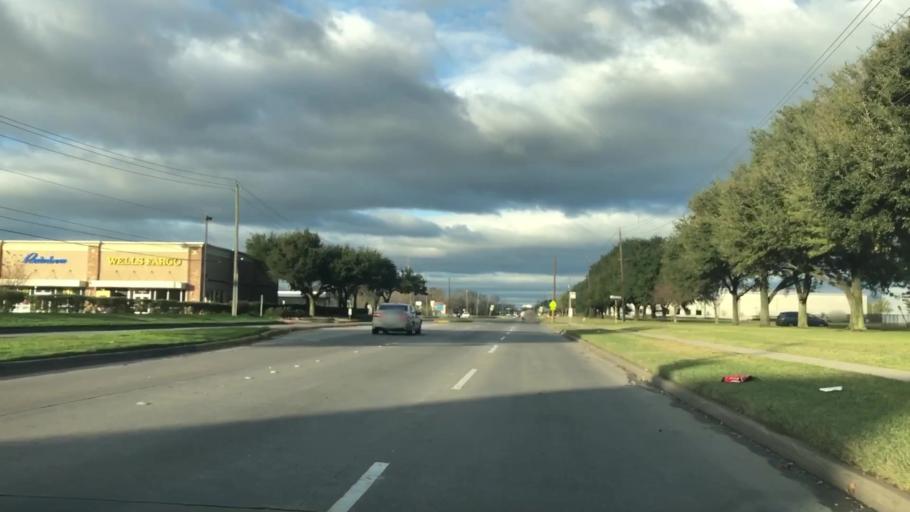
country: US
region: Texas
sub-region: Harris County
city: Aldine
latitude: 29.9152
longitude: -95.4156
